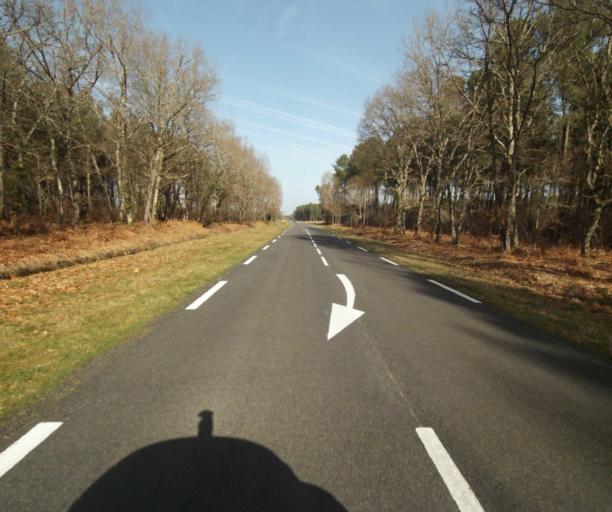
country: FR
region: Aquitaine
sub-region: Departement de la Gironde
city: Grignols
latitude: 44.1973
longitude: -0.1380
